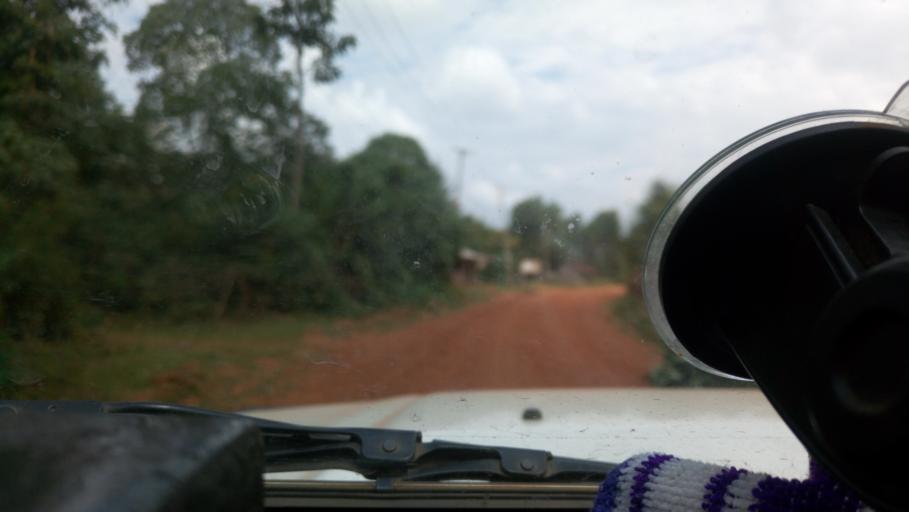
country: KE
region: Kericho
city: Litein
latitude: -0.6133
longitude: 35.1319
